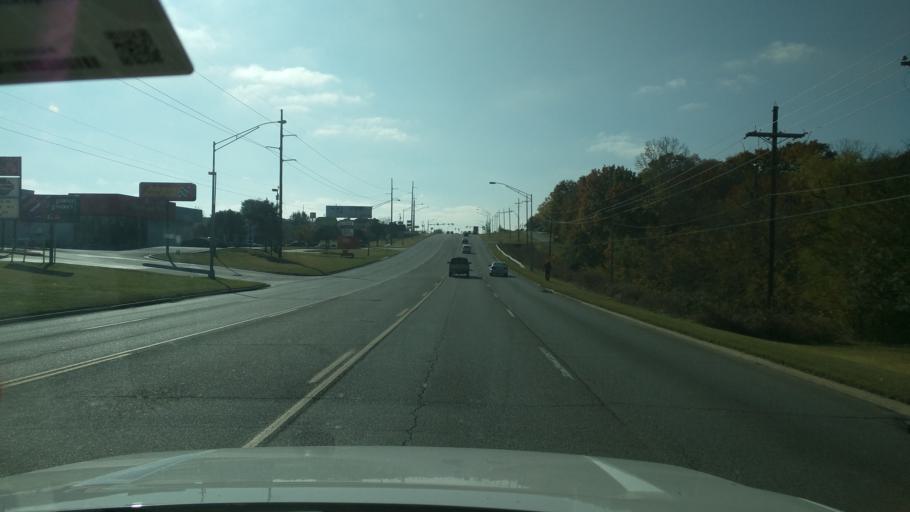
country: US
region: Oklahoma
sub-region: Washington County
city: Bartlesville
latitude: 36.7328
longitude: -95.9353
